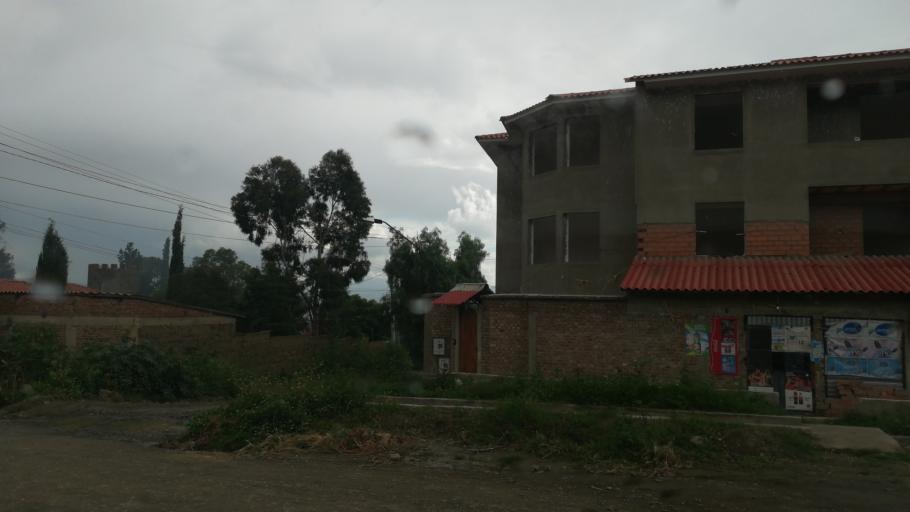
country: BO
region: Cochabamba
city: Cochabamba
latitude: -17.3365
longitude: -66.1995
